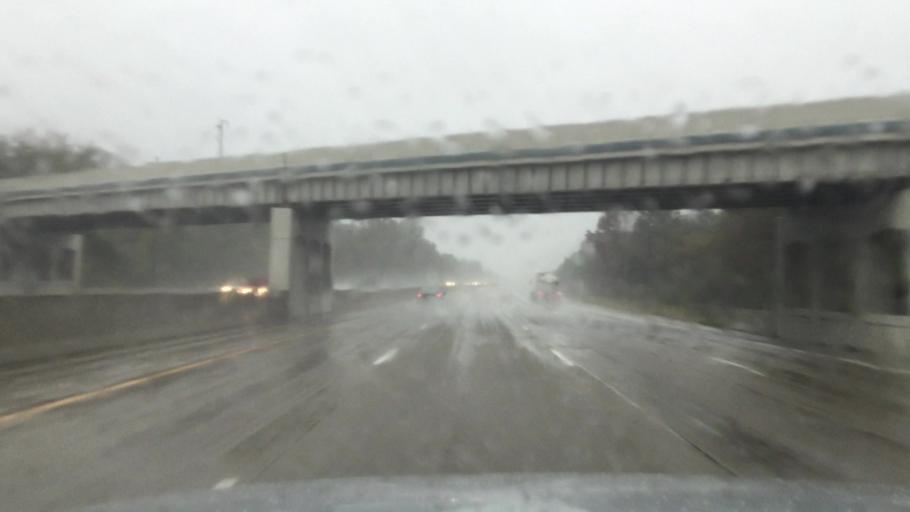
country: US
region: Michigan
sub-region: Saginaw County
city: Birch Run
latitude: 43.3071
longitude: -83.8354
